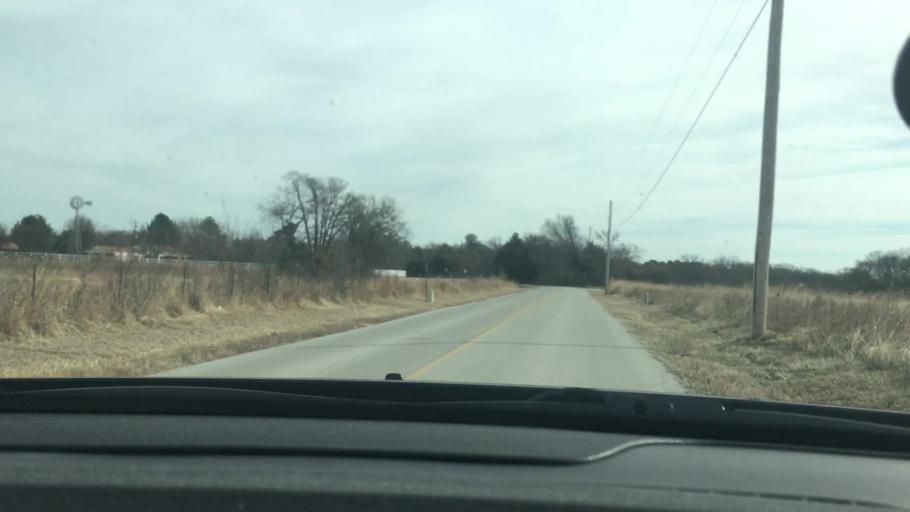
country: US
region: Oklahoma
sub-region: Carter County
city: Ardmore
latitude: 34.1733
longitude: -97.0803
